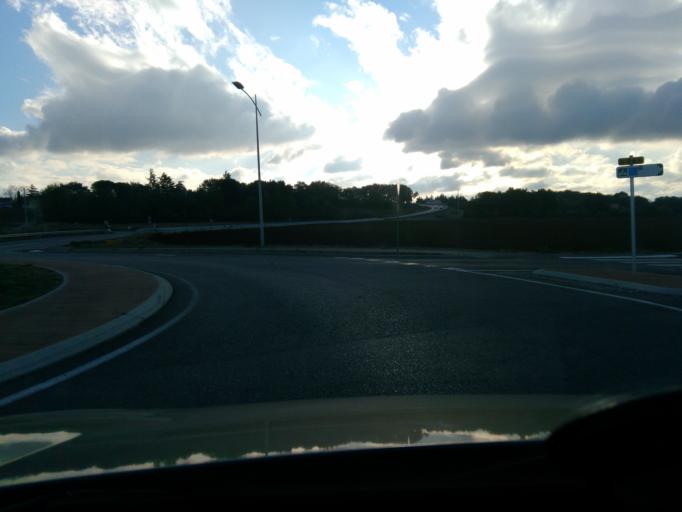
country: FR
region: Rhone-Alpes
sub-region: Departement de la Drome
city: Savasse
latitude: 44.5854
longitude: 4.7593
